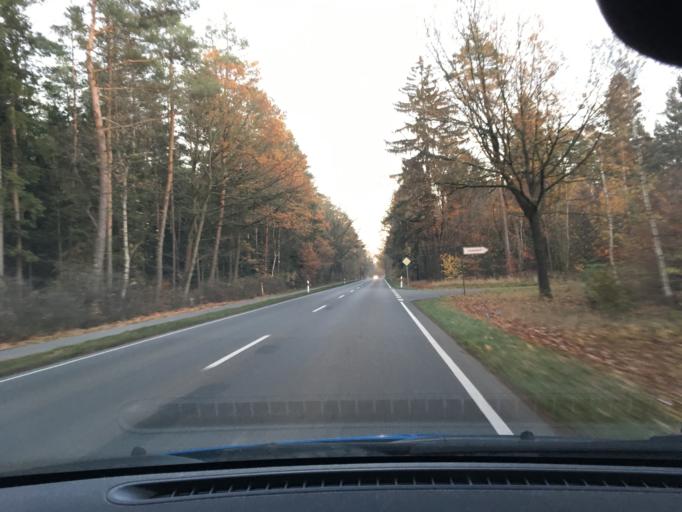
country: DE
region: Lower Saxony
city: Schwienau
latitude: 52.9992
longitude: 10.4763
